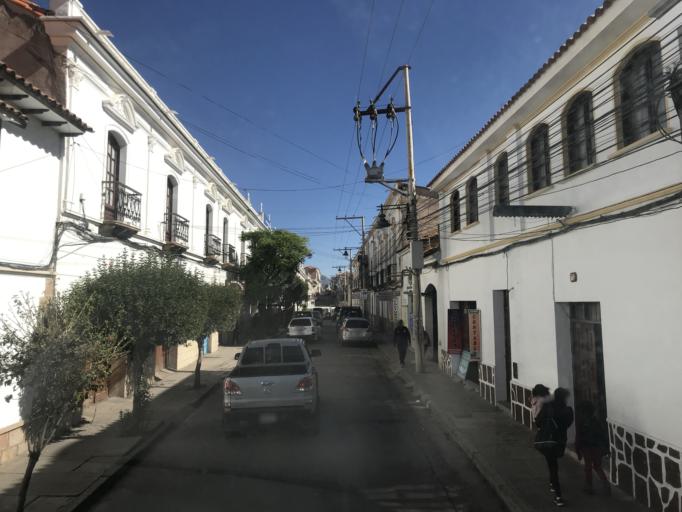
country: BO
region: Chuquisaca
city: Sucre
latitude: -19.0468
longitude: -65.2563
